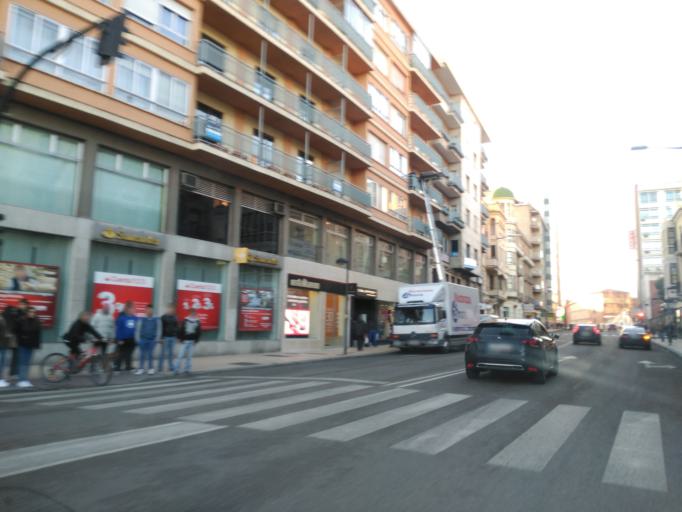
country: ES
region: Castille and Leon
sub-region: Provincia de Zamora
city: Zamora
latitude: 41.5073
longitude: -5.7412
